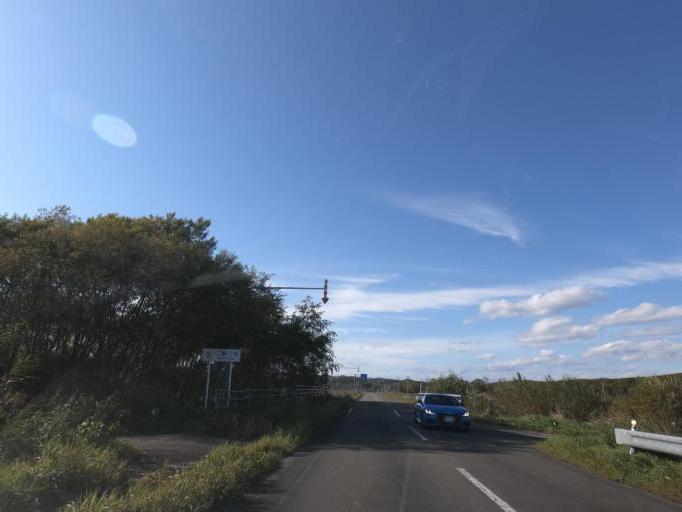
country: JP
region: Hokkaido
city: Obihiro
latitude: 42.6403
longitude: 143.5086
